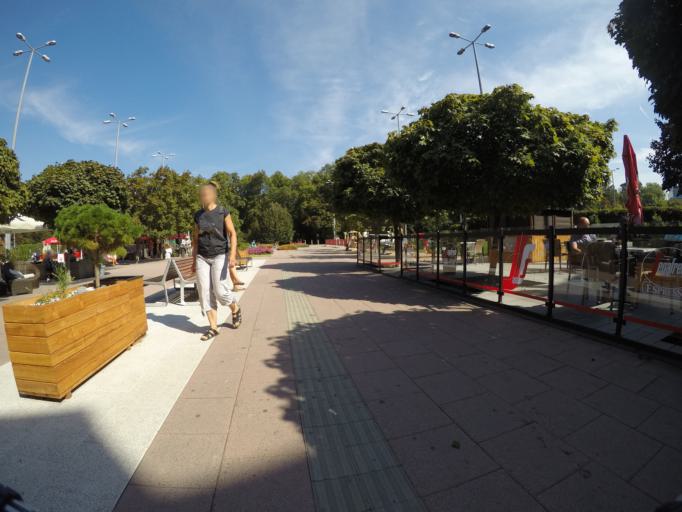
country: SK
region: Bratislavsky
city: Bratislava
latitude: 48.1332
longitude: 17.1083
